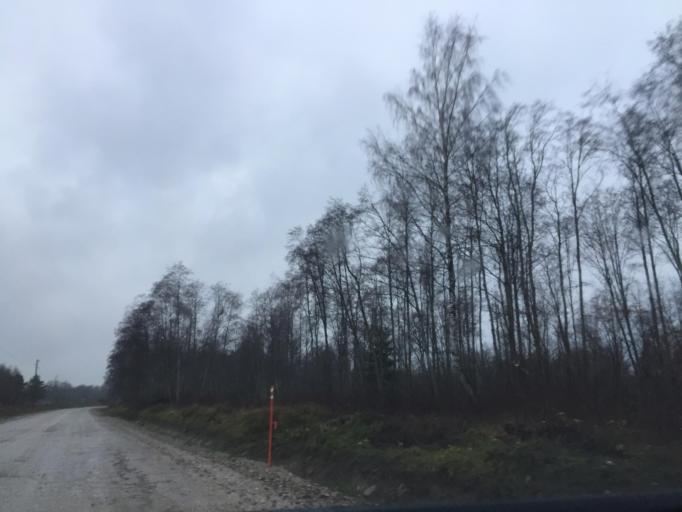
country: LV
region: Salacgrivas
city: Salacgriva
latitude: 57.7666
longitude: 24.4709
